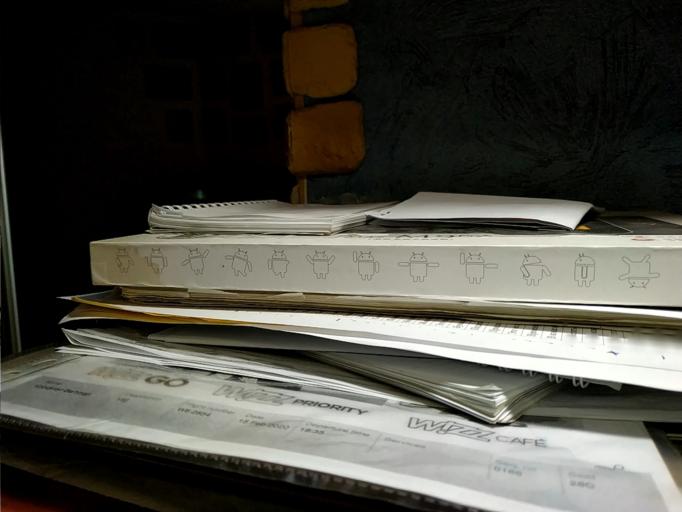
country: RU
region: Tverskaya
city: Toropets
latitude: 56.9028
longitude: 31.7773
